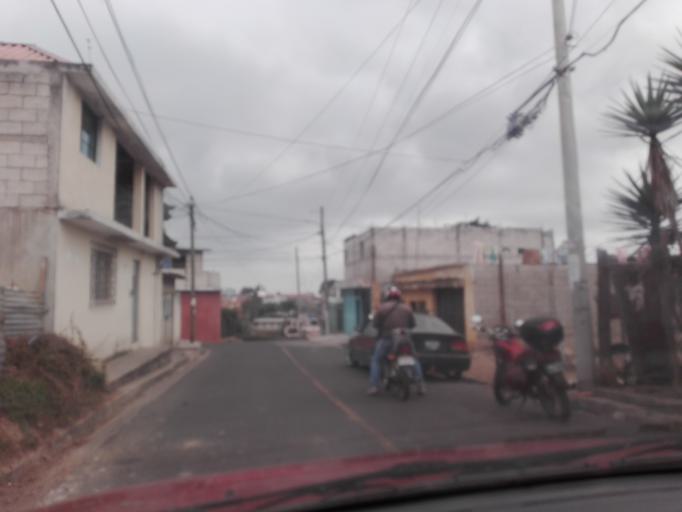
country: GT
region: Guatemala
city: San Jose Pinula
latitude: 14.5714
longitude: -90.4459
